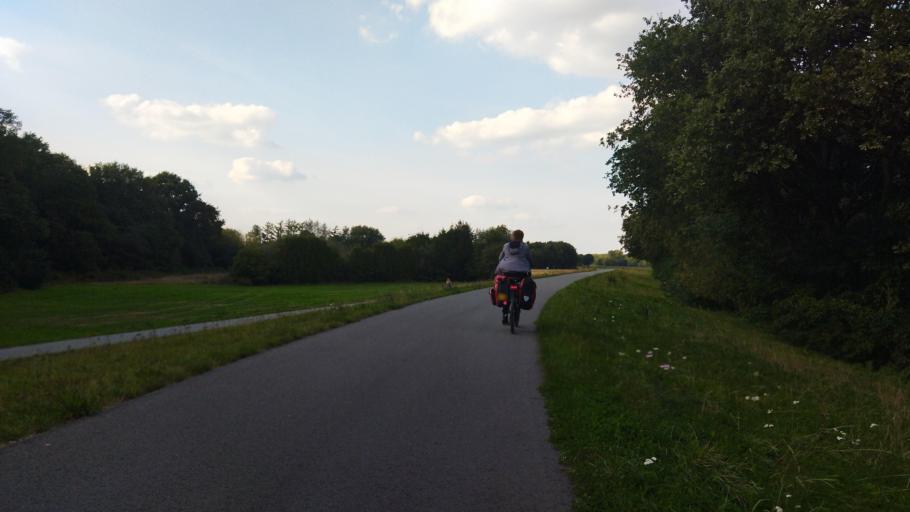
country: DE
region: Lower Saxony
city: Heede
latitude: 52.9958
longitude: 7.3127
